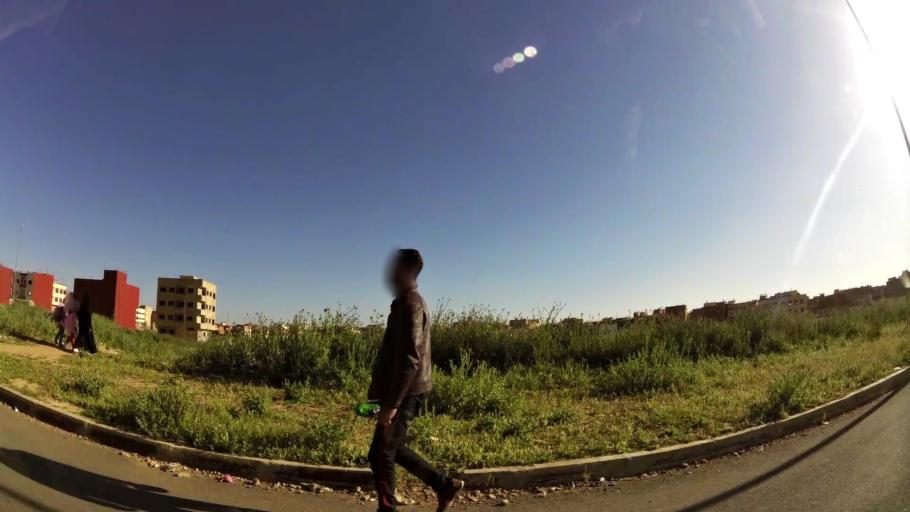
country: MA
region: Meknes-Tafilalet
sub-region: Meknes
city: Meknes
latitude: 33.8861
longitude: -5.5075
